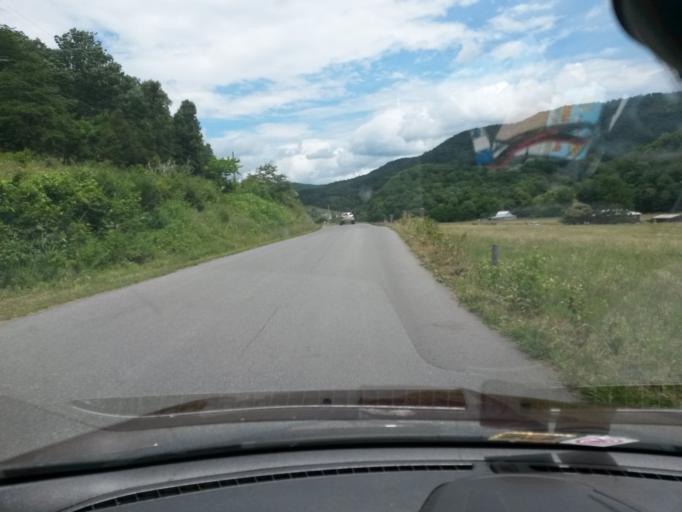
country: US
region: West Virginia
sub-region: Monroe County
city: Union
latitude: 37.5010
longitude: -80.5929
